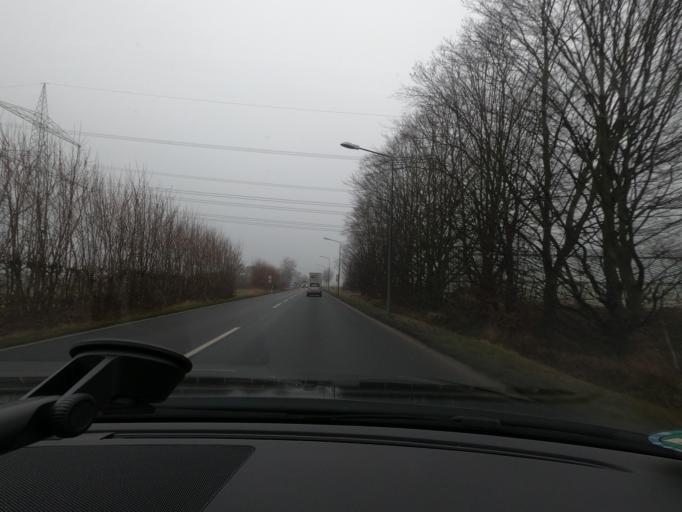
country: DE
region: North Rhine-Westphalia
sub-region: Regierungsbezirk Koln
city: Merzenich
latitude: 50.8149
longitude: 6.5208
